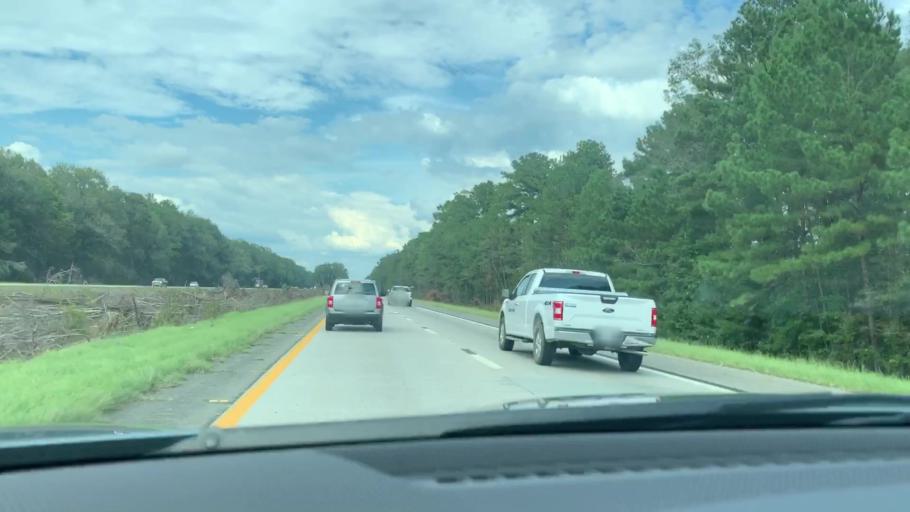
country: US
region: South Carolina
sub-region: Jasper County
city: Ridgeland
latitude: 32.3864
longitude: -81.0256
